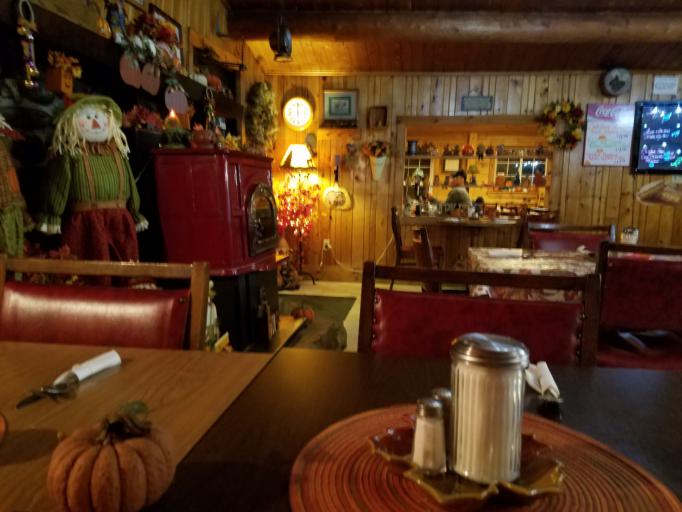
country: US
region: Maine
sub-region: Aroostook County
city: Hodgdon
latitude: 46.1127
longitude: -68.1628
